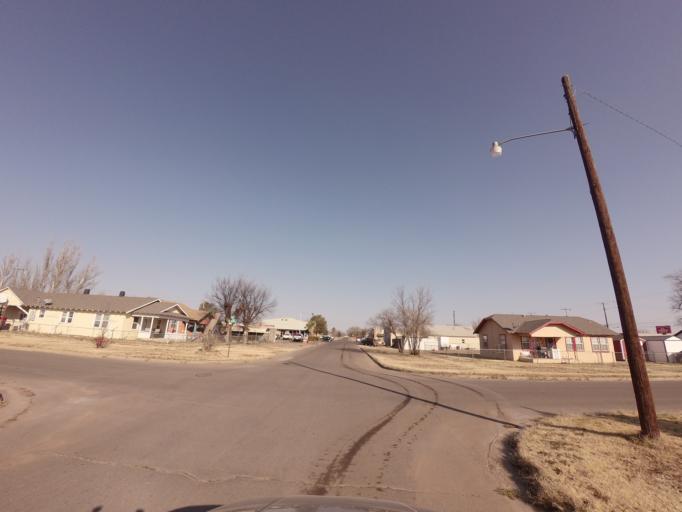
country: US
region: New Mexico
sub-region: Curry County
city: Clovis
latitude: 34.4038
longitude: -103.2117
